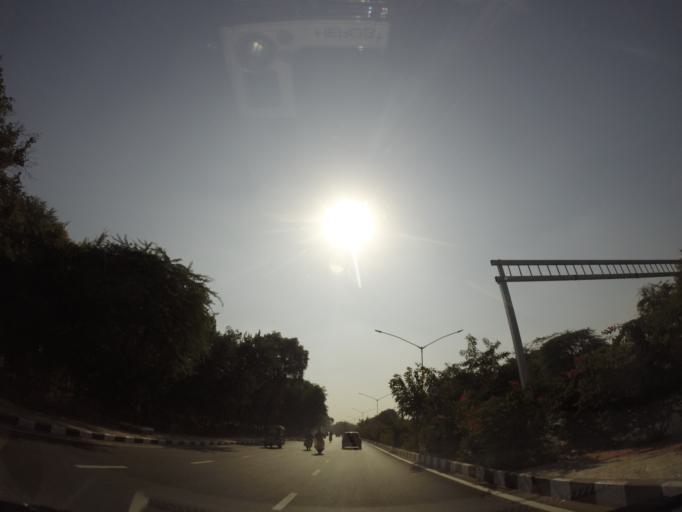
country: IN
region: Gujarat
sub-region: Gandhinagar
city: Ghandinagar
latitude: 23.2037
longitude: 72.6331
